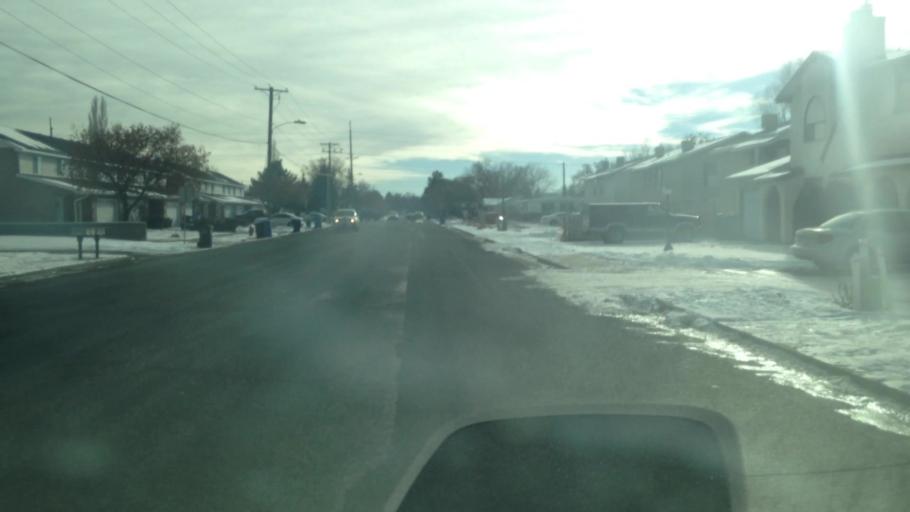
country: US
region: Utah
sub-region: Cache County
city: Logan
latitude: 41.7517
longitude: -111.8394
